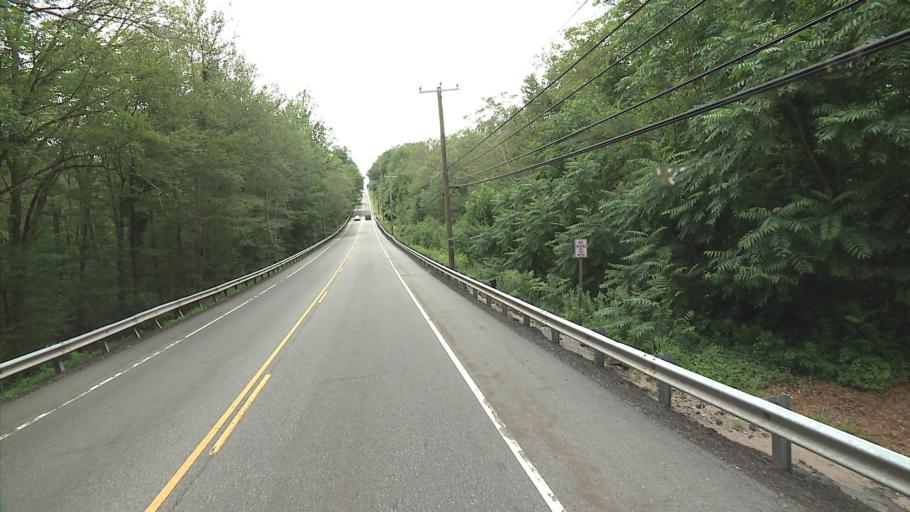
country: US
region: Connecticut
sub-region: New Haven County
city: Madison
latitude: 41.3616
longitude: -72.5990
